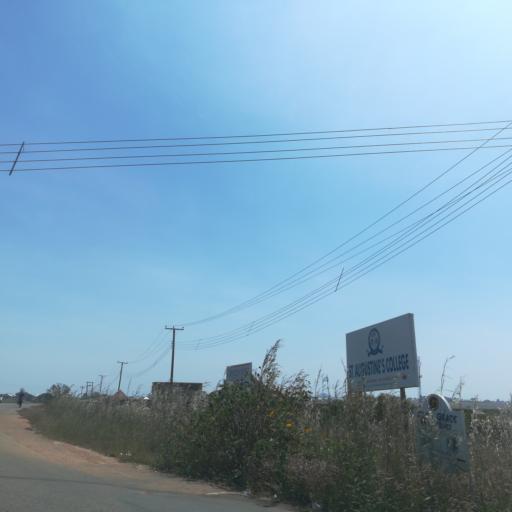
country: NG
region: Plateau
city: Bukuru
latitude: 9.8470
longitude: 8.9207
